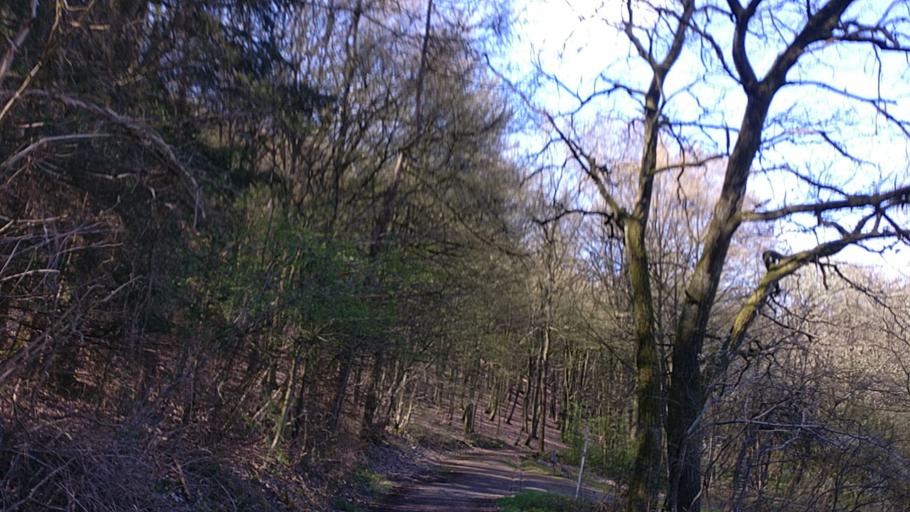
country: DE
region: Rheinland-Pfalz
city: Peterslahr
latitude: 50.6246
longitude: 7.4386
